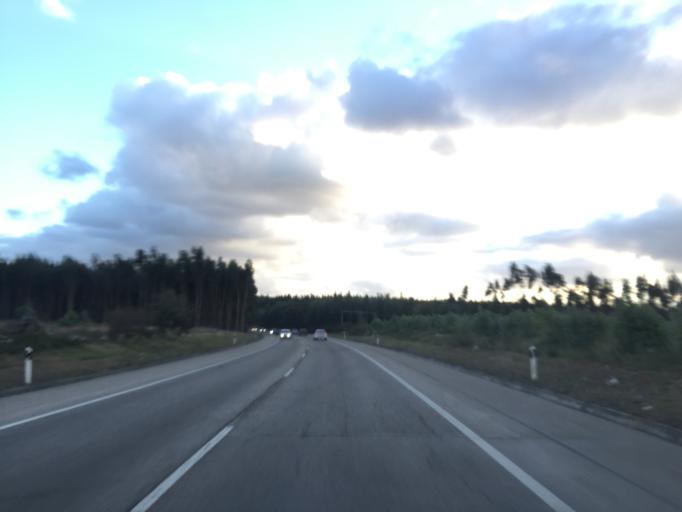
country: PT
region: Leiria
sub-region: Alcobaca
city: Benedita
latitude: 39.4201
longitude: -8.9626
